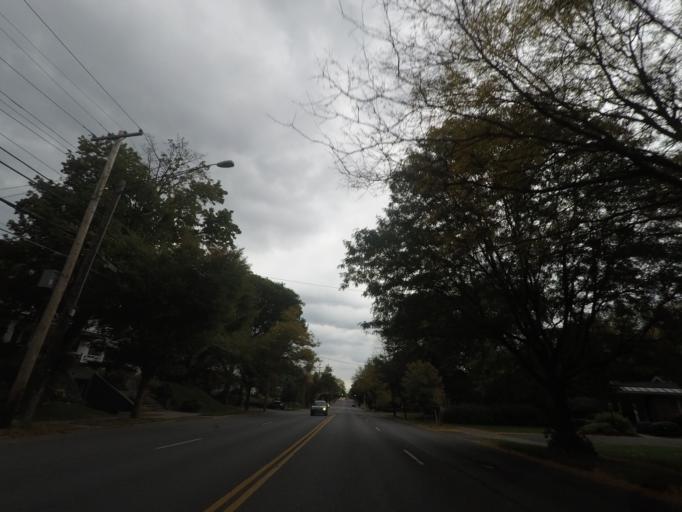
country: US
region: New York
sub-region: Albany County
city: West Albany
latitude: 42.6692
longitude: -73.8004
